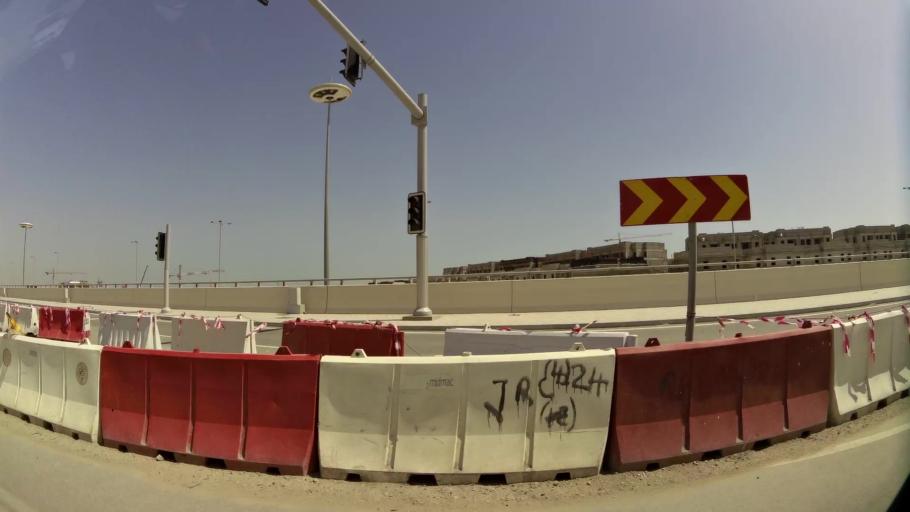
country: QA
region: Baladiyat Umm Salal
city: Umm Salal Muhammad
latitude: 25.4048
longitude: 51.5130
